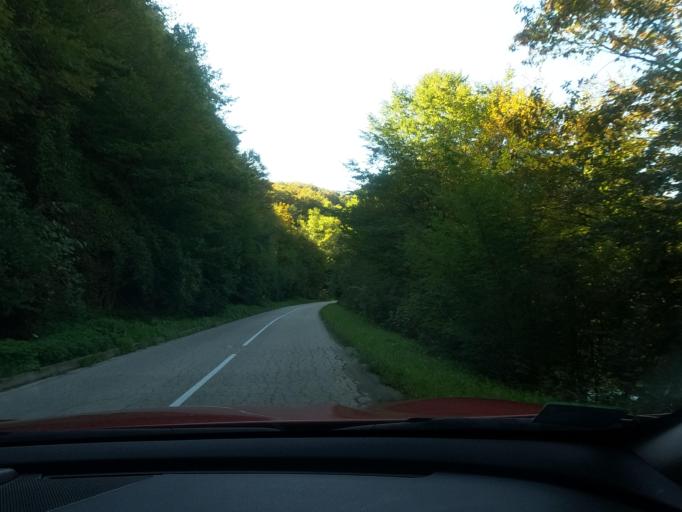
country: BA
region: Federation of Bosnia and Herzegovina
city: Vrnograc
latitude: 45.2655
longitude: 15.9712
